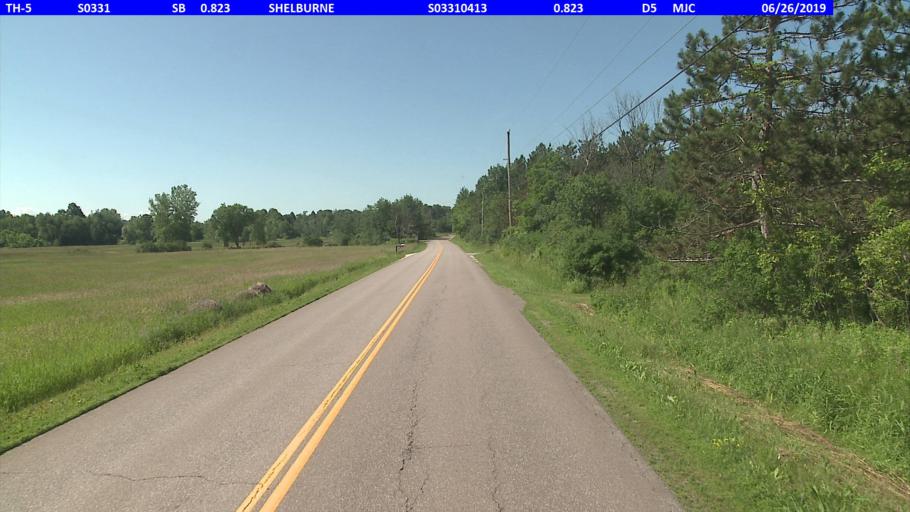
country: US
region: Vermont
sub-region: Chittenden County
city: South Burlington
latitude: 44.3828
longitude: -73.1770
